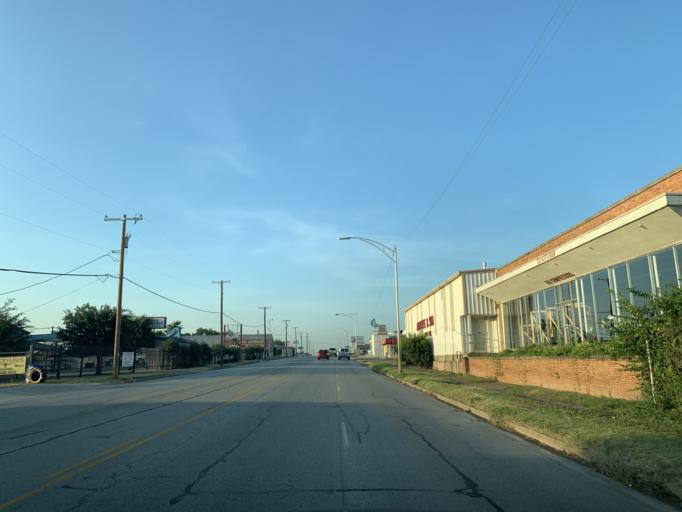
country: US
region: Texas
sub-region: Tarrant County
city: Blue Mound
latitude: 32.8089
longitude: -97.3515
